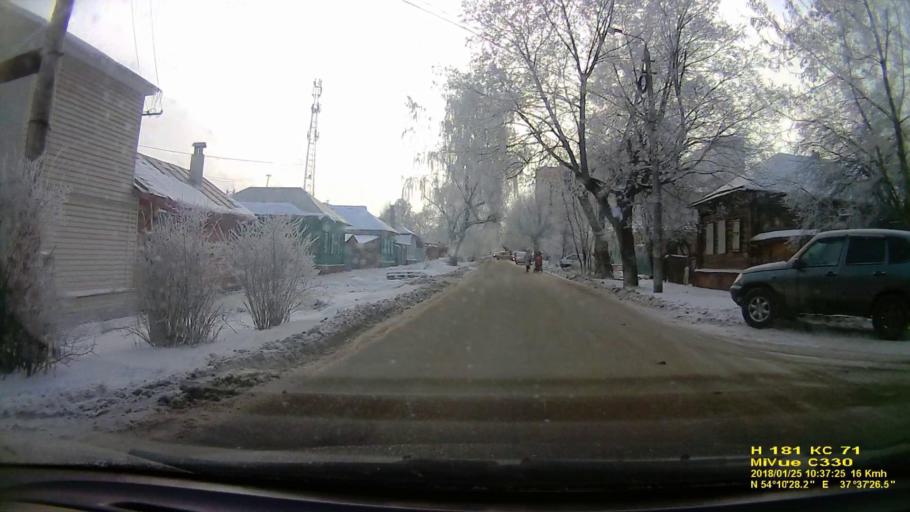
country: RU
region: Tula
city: Tula
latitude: 54.1746
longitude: 37.6238
